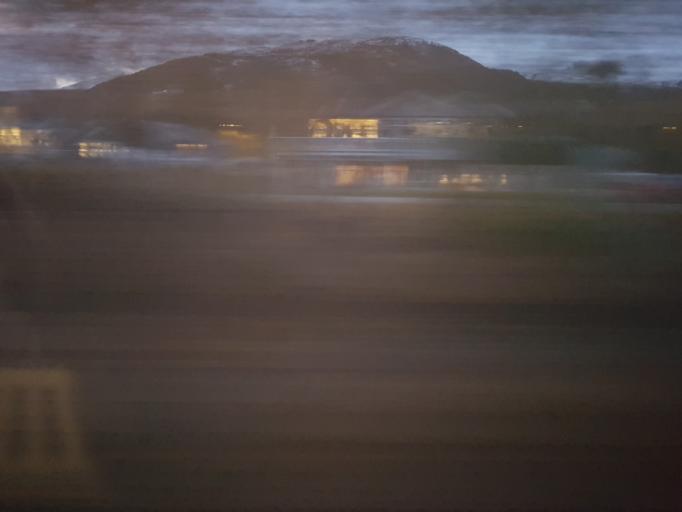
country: NO
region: Sor-Trondelag
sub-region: Oppdal
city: Oppdal
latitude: 62.5975
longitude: 9.7106
